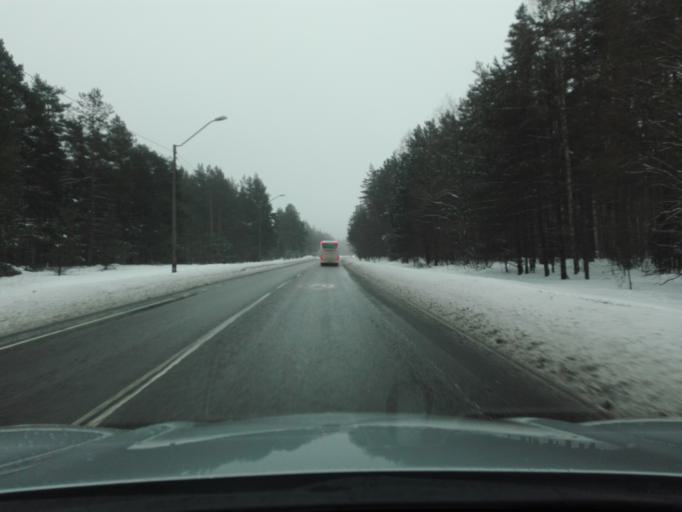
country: EE
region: Harju
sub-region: Tallinna linn
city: Tallinn
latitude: 59.3613
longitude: 24.7658
